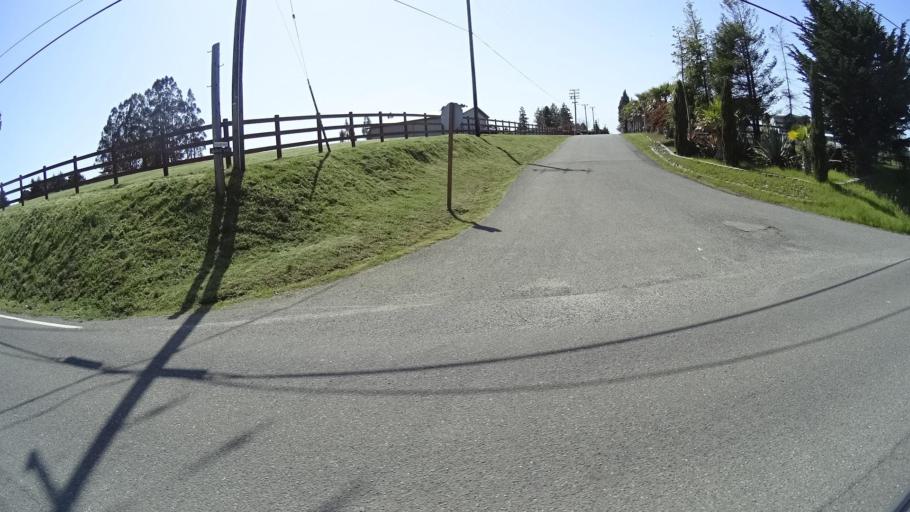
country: US
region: California
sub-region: Humboldt County
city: Hydesville
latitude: 40.5582
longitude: -124.1231
